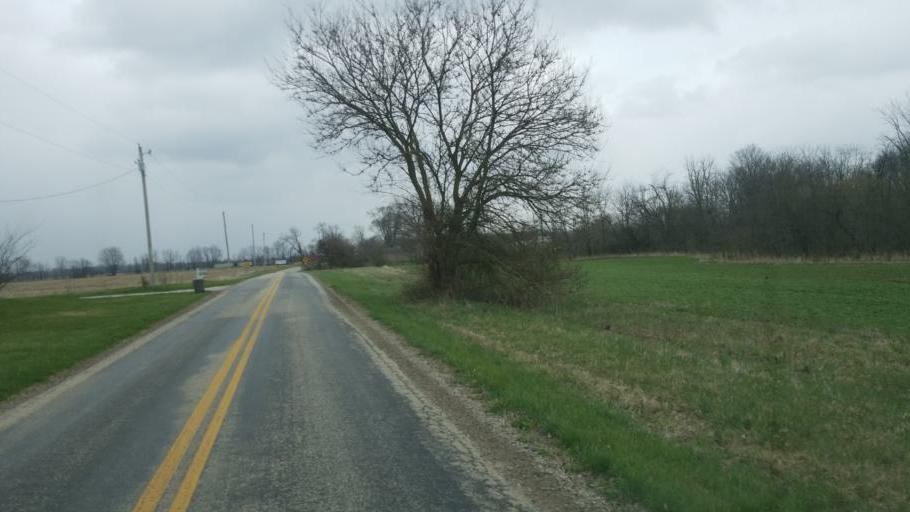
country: US
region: Ohio
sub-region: Marion County
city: Prospect
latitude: 40.4022
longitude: -83.2167
